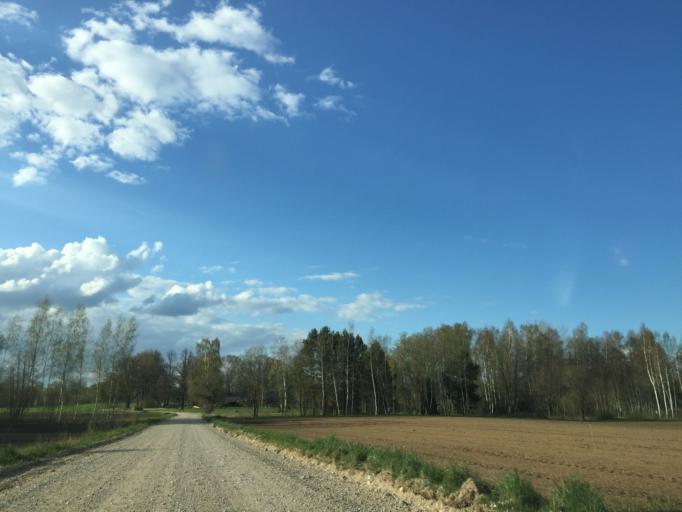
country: LV
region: Beverina
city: Murmuiza
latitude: 57.3932
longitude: 25.4791
